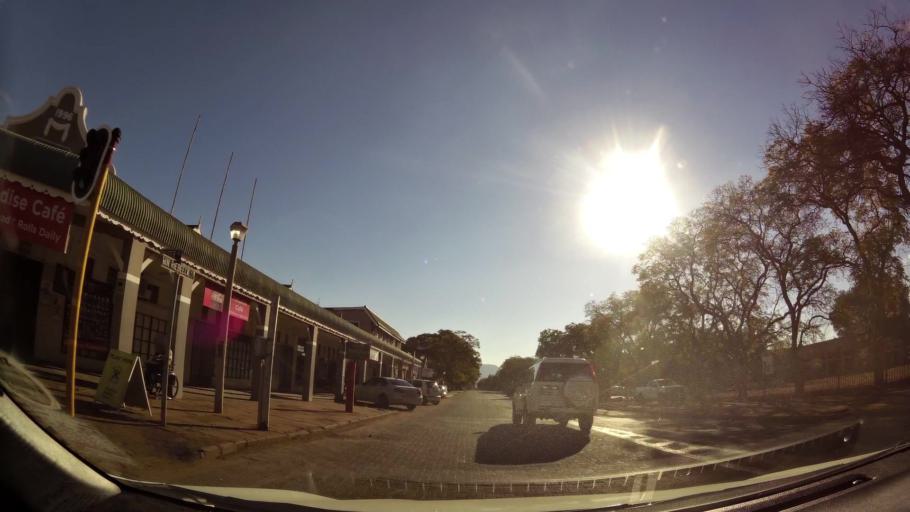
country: ZA
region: Limpopo
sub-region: Waterberg District Municipality
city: Mokopane
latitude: -24.1853
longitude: 29.0100
